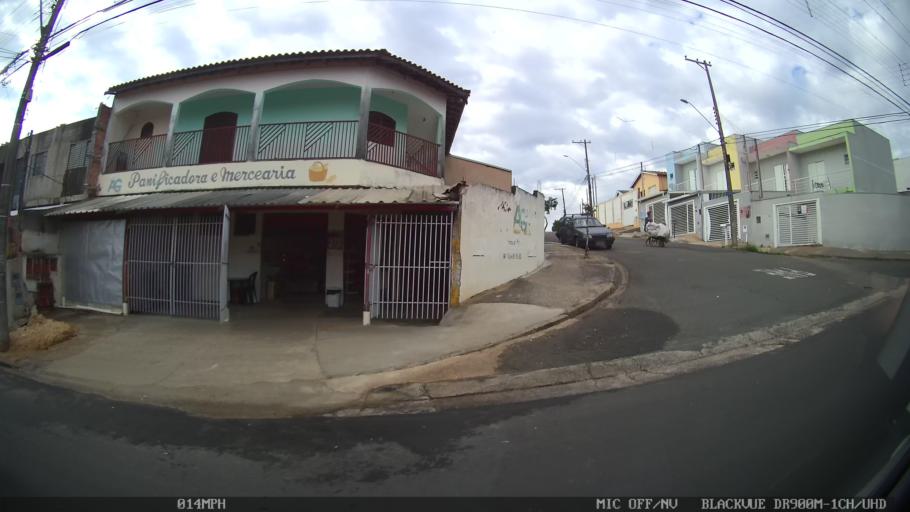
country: BR
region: Sao Paulo
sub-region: Americana
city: Americana
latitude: -22.7276
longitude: -47.3537
